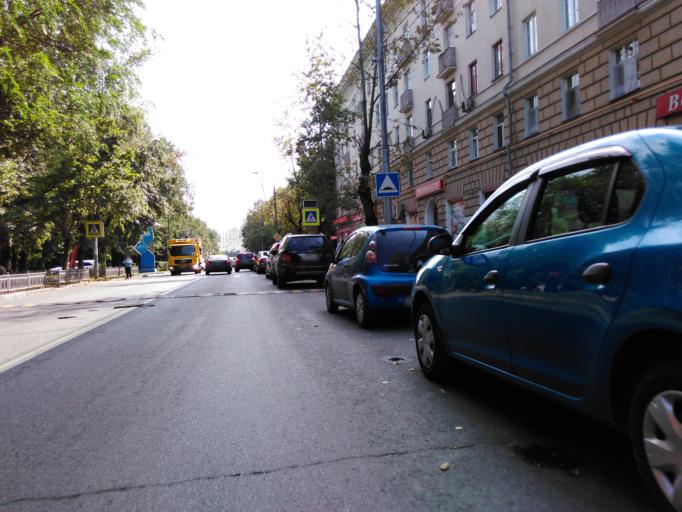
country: RU
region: Moskovskaya
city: Bol'shaya Setun'
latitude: 55.7194
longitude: 37.4014
